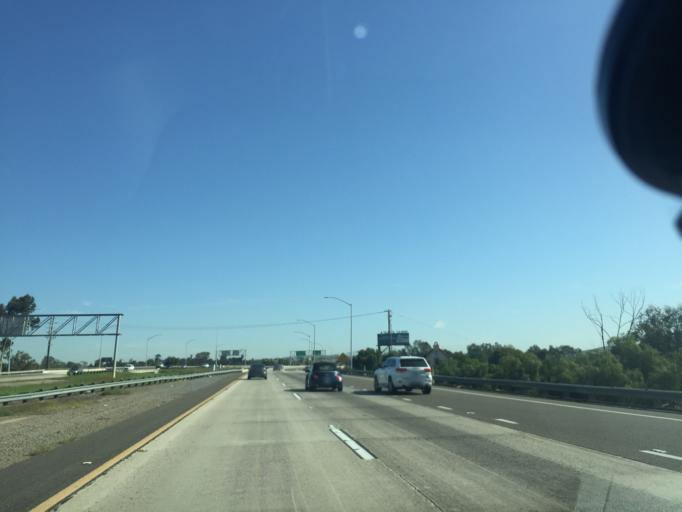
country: US
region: California
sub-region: San Diego County
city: Imperial Beach
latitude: 32.5672
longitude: -117.0683
